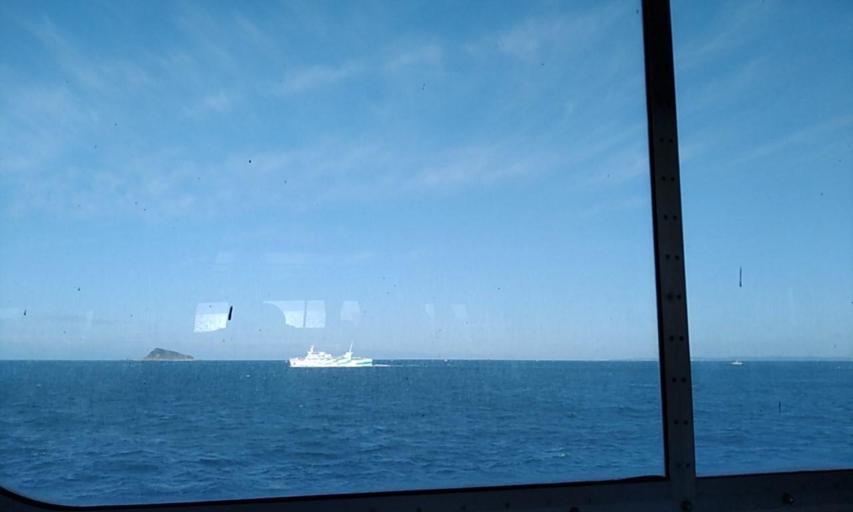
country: JP
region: Mie
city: Toba
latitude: 34.5356
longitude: 136.9513
